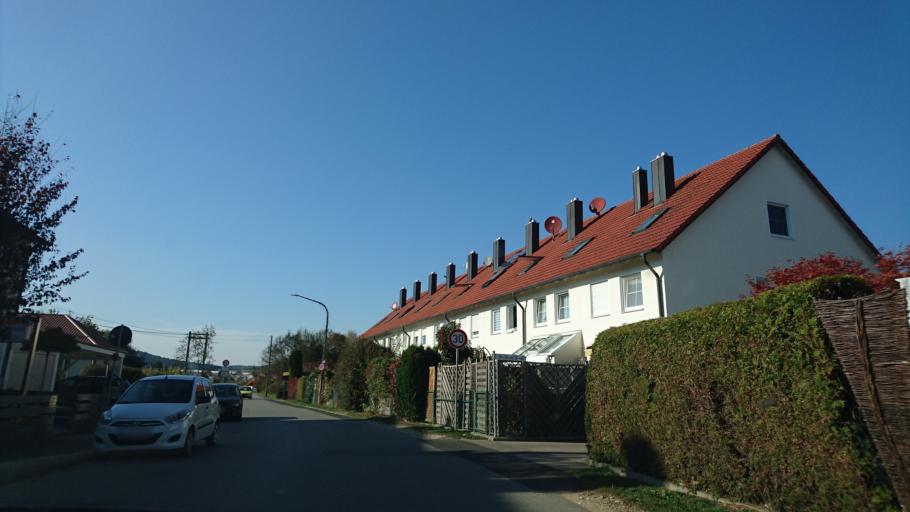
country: DE
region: Bavaria
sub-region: Swabia
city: Zusmarshausen
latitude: 48.4051
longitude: 10.5974
